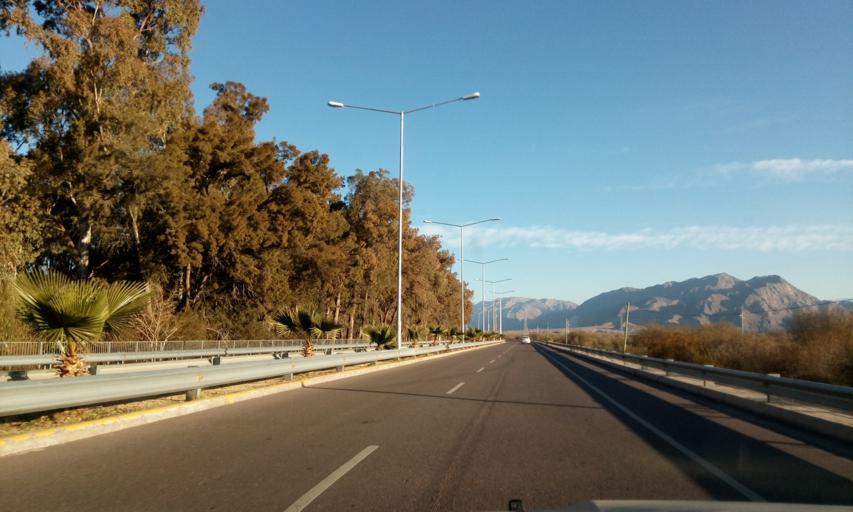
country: AR
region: San Juan
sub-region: Departamento de Rivadavia
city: Rivadavia
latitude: -31.5068
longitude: -68.6448
